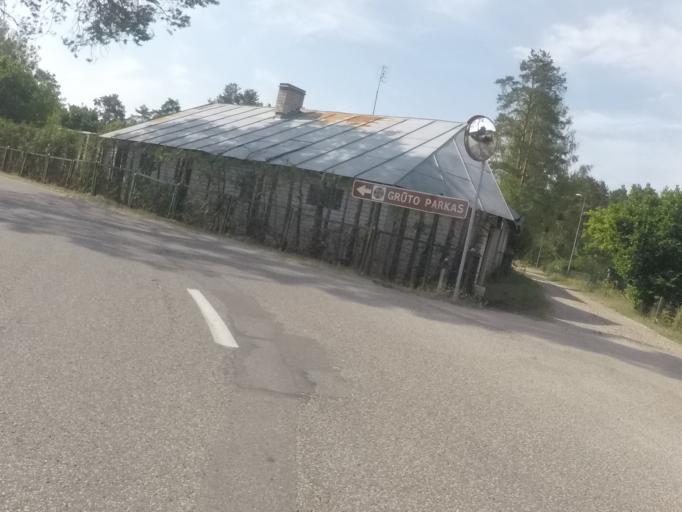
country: LT
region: Alytaus apskritis
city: Druskininkai
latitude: 54.0313
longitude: 24.0749
